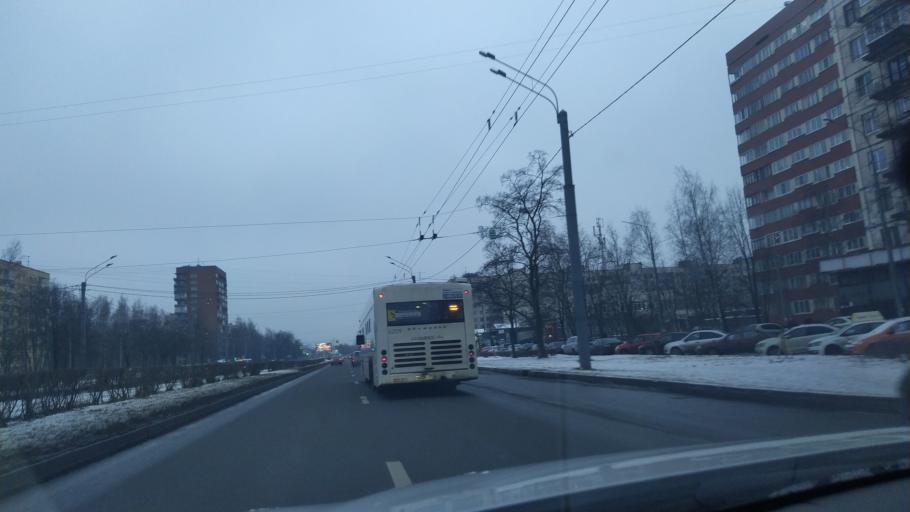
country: RU
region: St.-Petersburg
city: Grazhdanka
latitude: 60.0361
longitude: 30.3957
